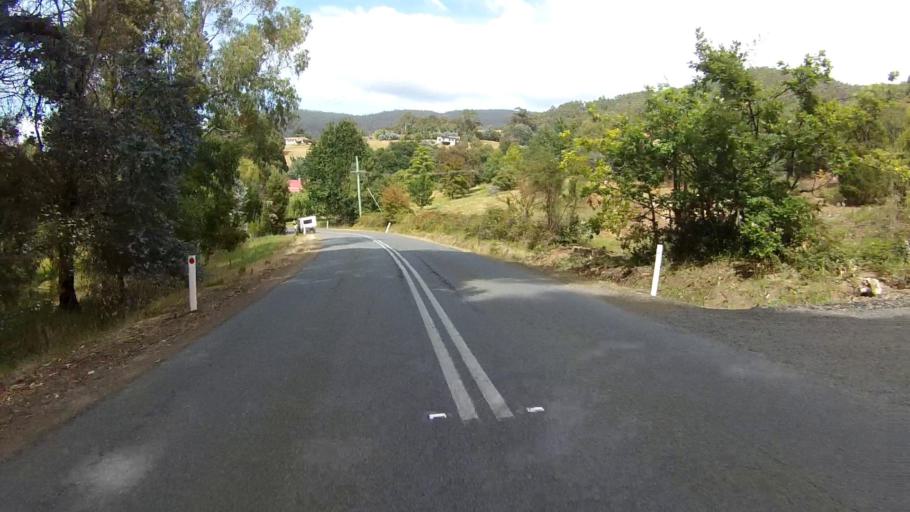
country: AU
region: Tasmania
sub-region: Kingborough
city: Kettering
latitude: -43.2072
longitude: 147.2551
